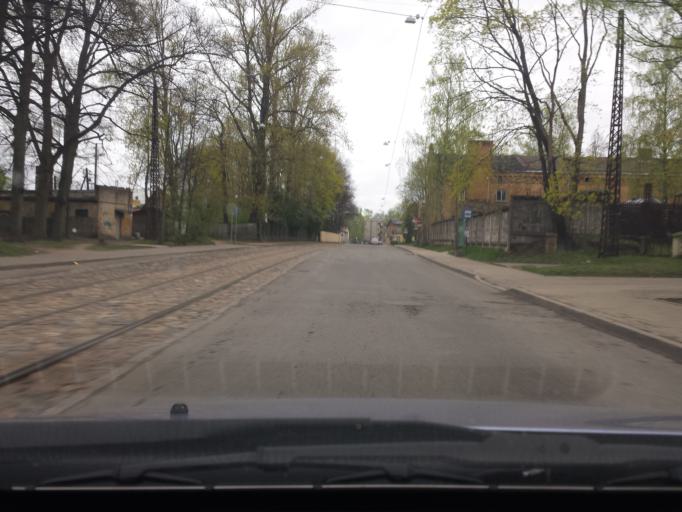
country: LV
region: Riga
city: Riga
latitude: 56.9569
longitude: 24.0625
